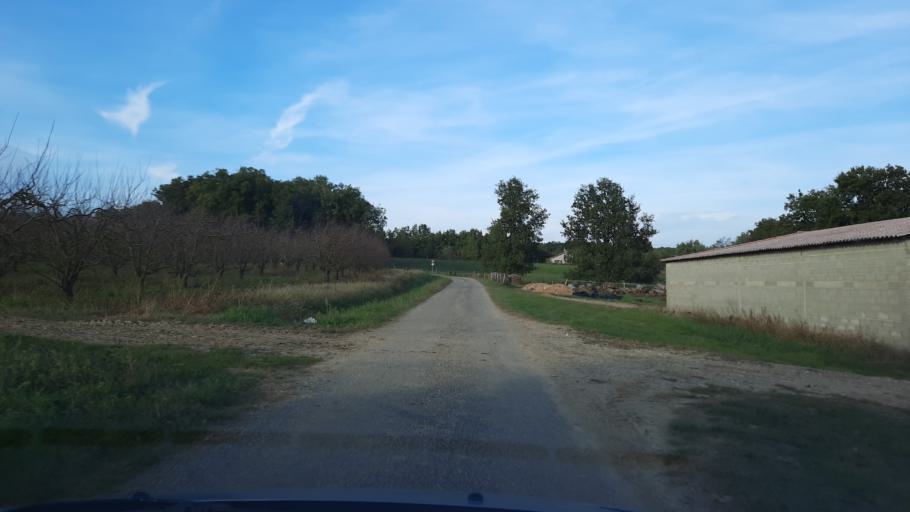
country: FR
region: Midi-Pyrenees
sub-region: Departement du Tarn-et-Garonne
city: Molieres
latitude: 44.1857
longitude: 1.3133
